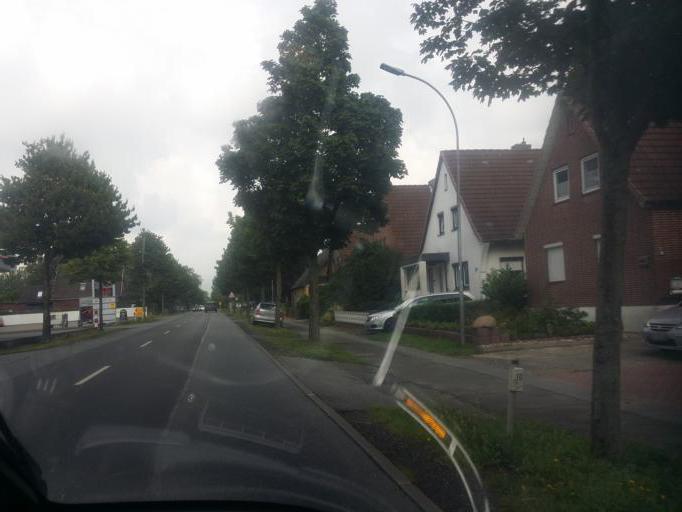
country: DE
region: Schleswig-Holstein
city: Heide
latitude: 54.2083
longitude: 9.1098
